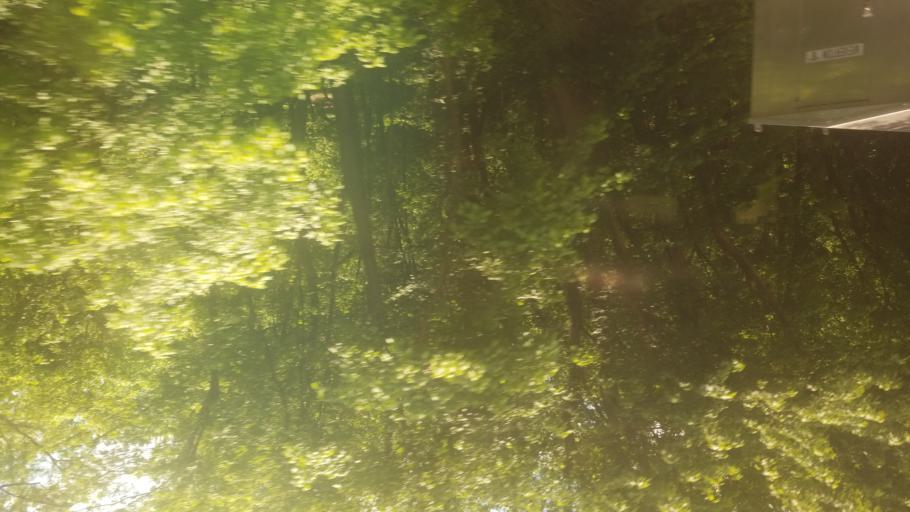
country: US
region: Maryland
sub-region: Frederick County
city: Brunswick
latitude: 39.3300
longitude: -77.6740
